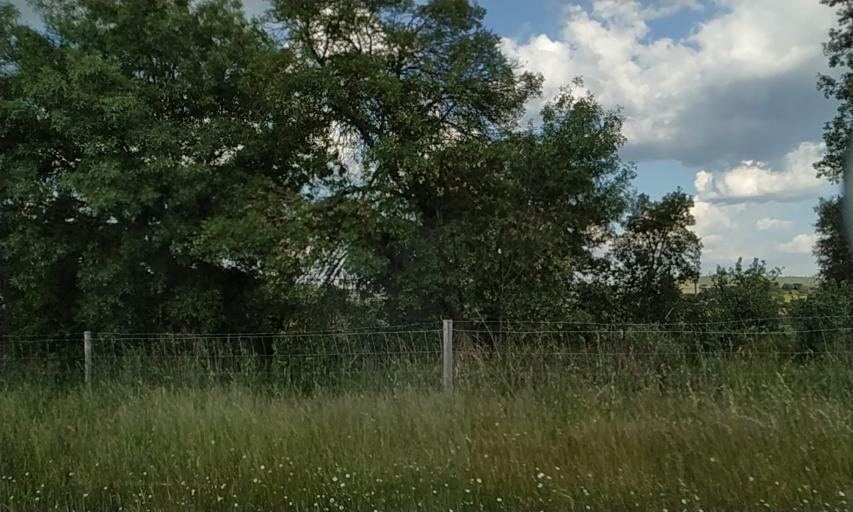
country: PT
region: Portalegre
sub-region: Portalegre
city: Urra
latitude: 39.2419
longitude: -7.4508
